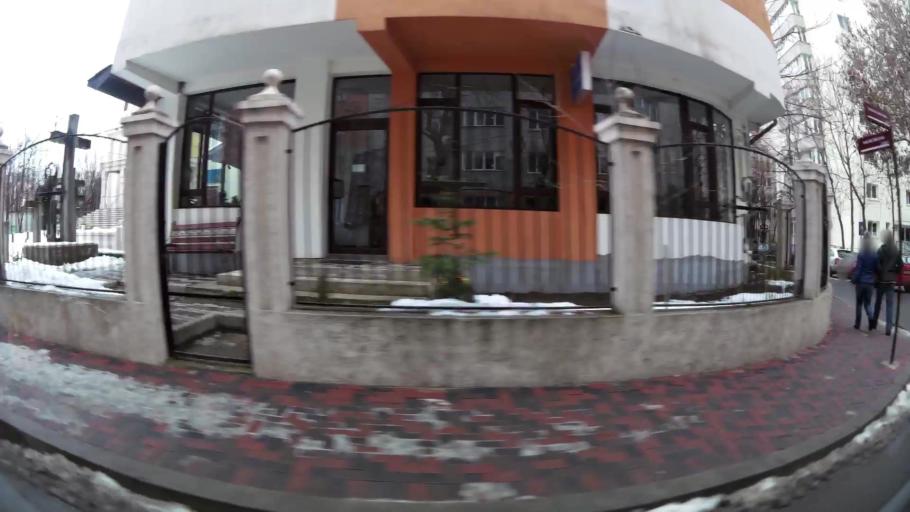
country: RO
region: Ilfov
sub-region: Comuna Popesti-Leordeni
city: Popesti-Leordeni
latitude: 44.4153
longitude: 26.1684
